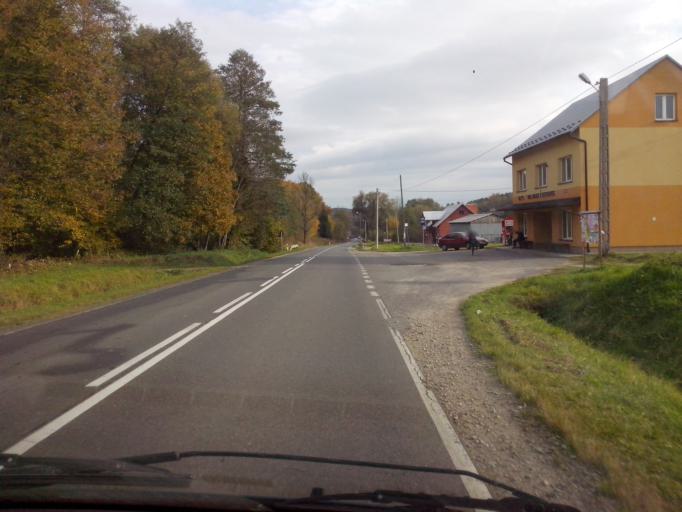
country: PL
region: Subcarpathian Voivodeship
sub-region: Powiat strzyzowski
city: Wisniowa
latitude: 49.9030
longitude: 21.6312
